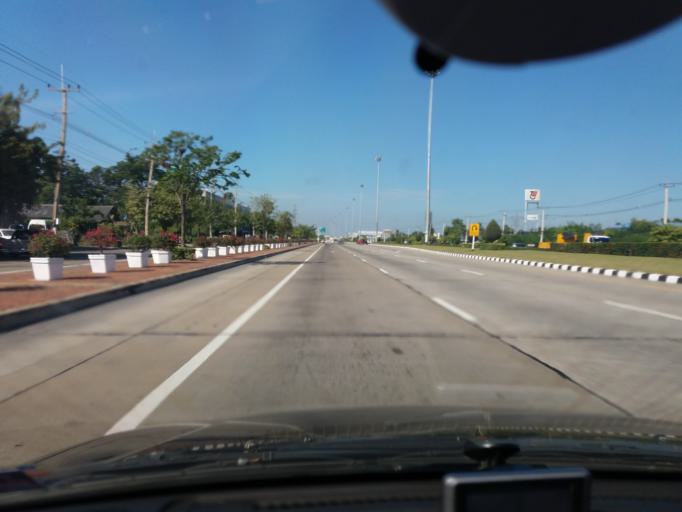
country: TH
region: Suphan Buri
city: Suphan Buri
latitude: 14.4857
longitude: 100.1314
